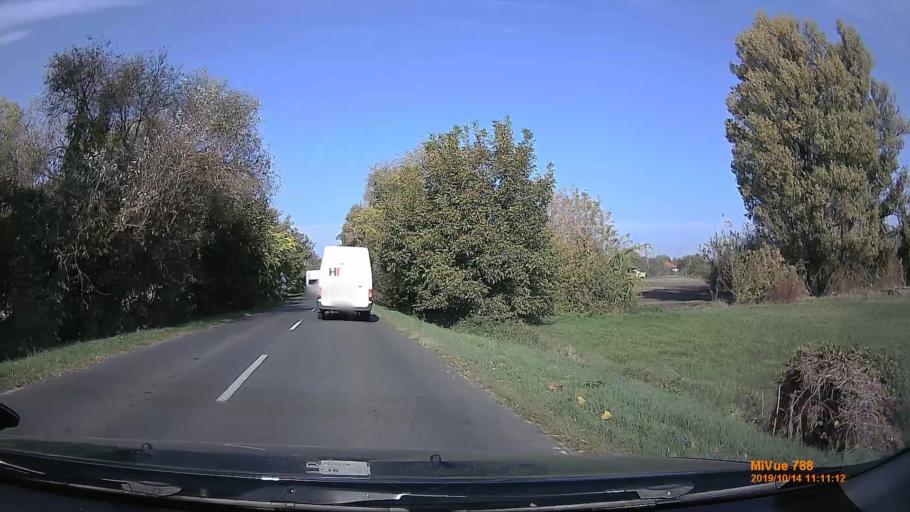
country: HU
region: Pest
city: Peteri
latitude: 47.3786
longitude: 19.4187
